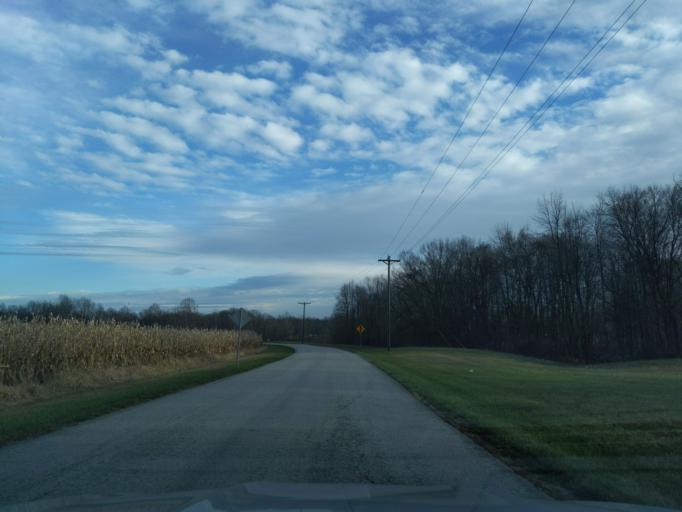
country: US
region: Indiana
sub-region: Decatur County
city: Greensburg
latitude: 39.2141
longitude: -85.4486
